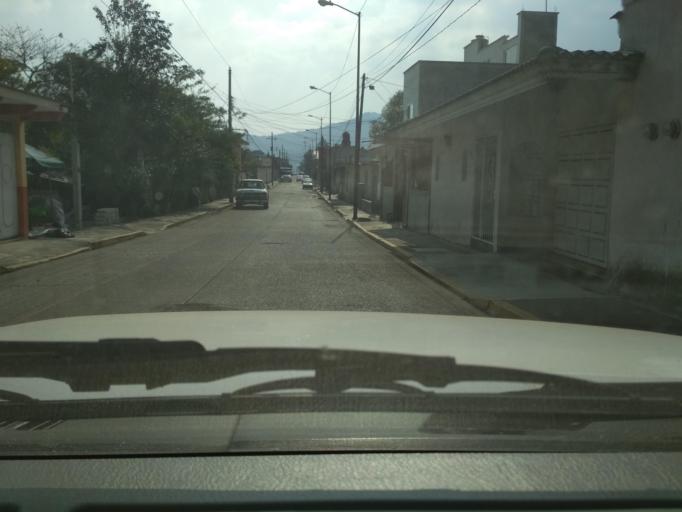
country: MX
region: Veracruz
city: Orizaba
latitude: 18.8699
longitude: -97.0935
